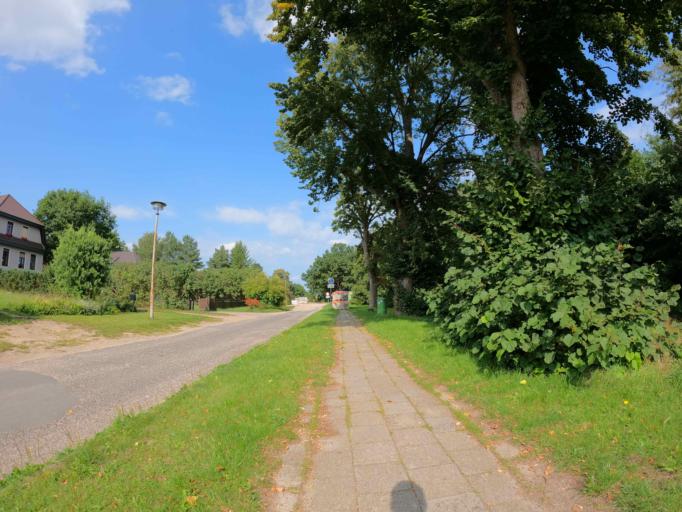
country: DE
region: Mecklenburg-Vorpommern
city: Malchow
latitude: 53.4833
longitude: 12.4378
